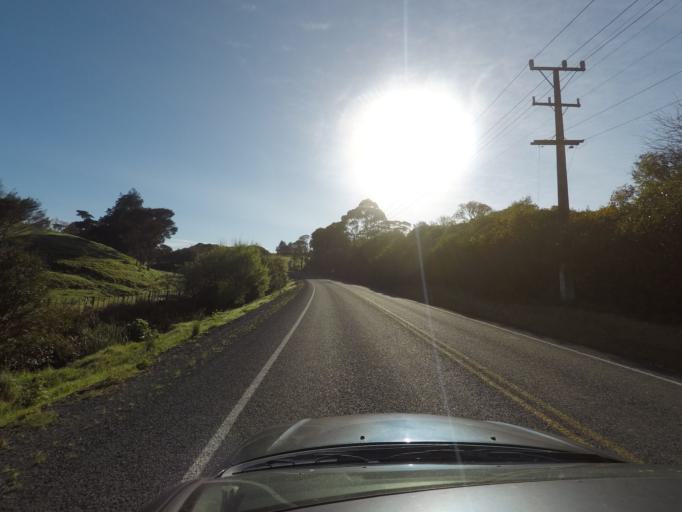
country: NZ
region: Auckland
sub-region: Auckland
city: Red Hill
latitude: -36.9959
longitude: 174.9823
